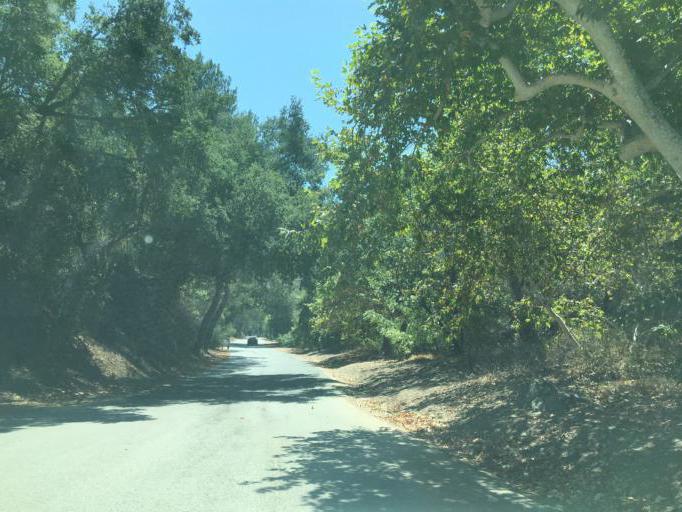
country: US
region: California
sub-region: Los Angeles County
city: Beverly Hills
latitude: 34.1106
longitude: -118.4153
